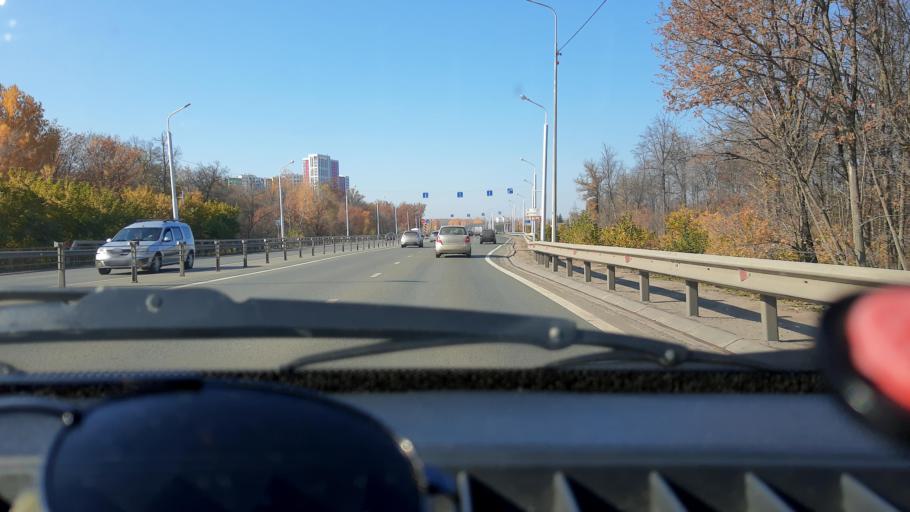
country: RU
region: Bashkortostan
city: Ufa
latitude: 54.6992
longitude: 55.8764
